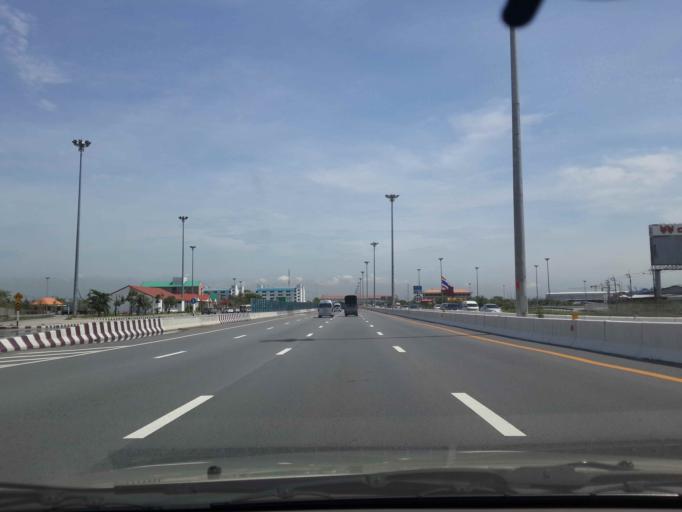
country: TH
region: Bangkok
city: Lat Krabang
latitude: 13.7012
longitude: 100.8244
